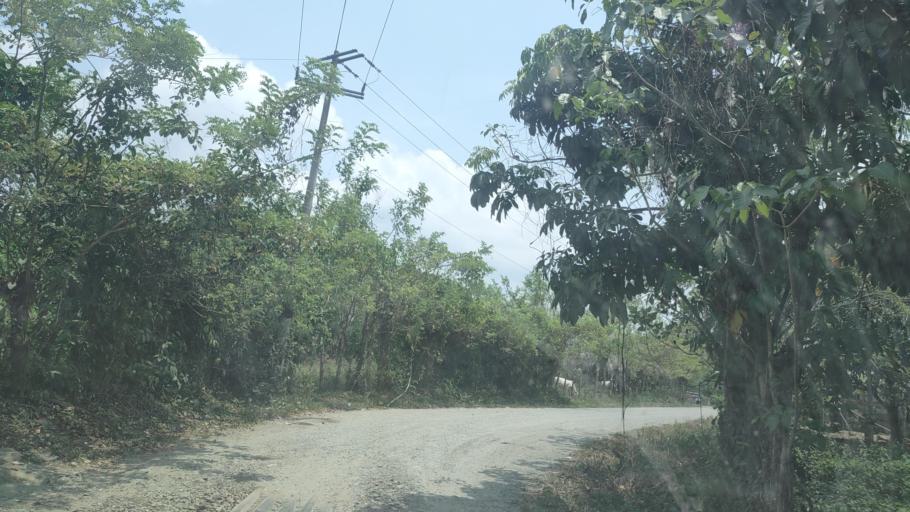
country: MX
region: Tabasco
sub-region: Huimanguillo
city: Francisco Rueda
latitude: 17.5852
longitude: -93.9593
